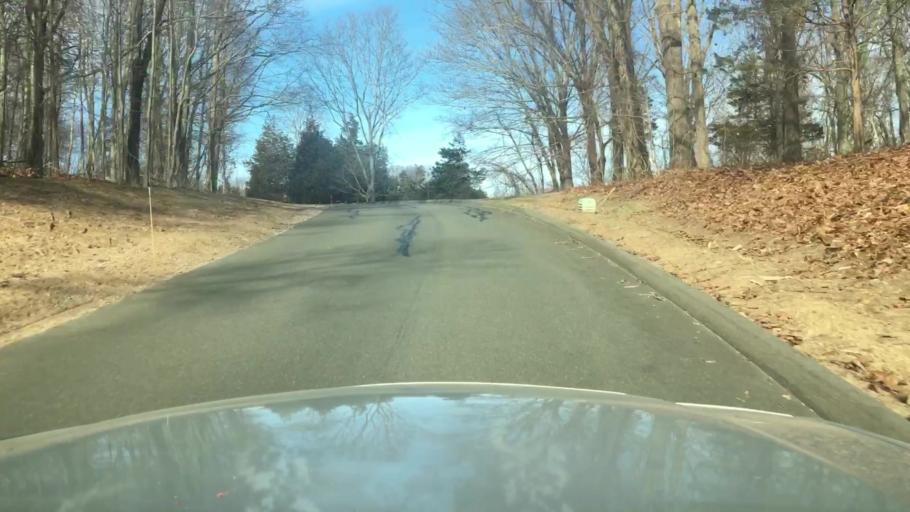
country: US
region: Connecticut
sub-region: Middlesex County
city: Essex Village
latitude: 41.3754
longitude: -72.3899
